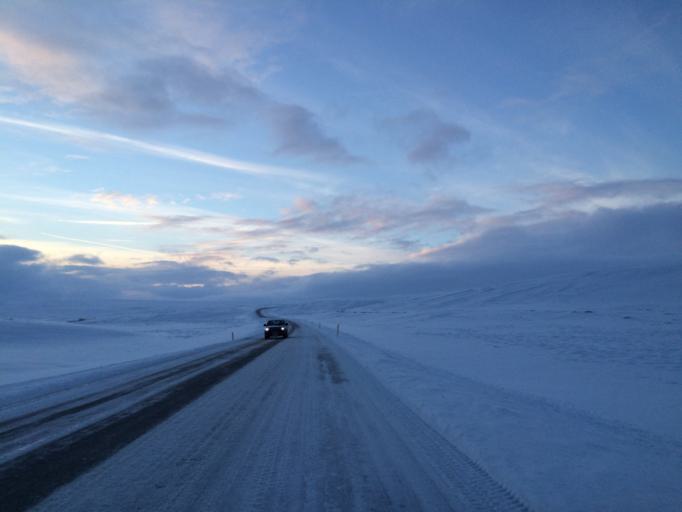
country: IS
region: South
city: Hveragerdi
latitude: 64.2289
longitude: -21.2032
